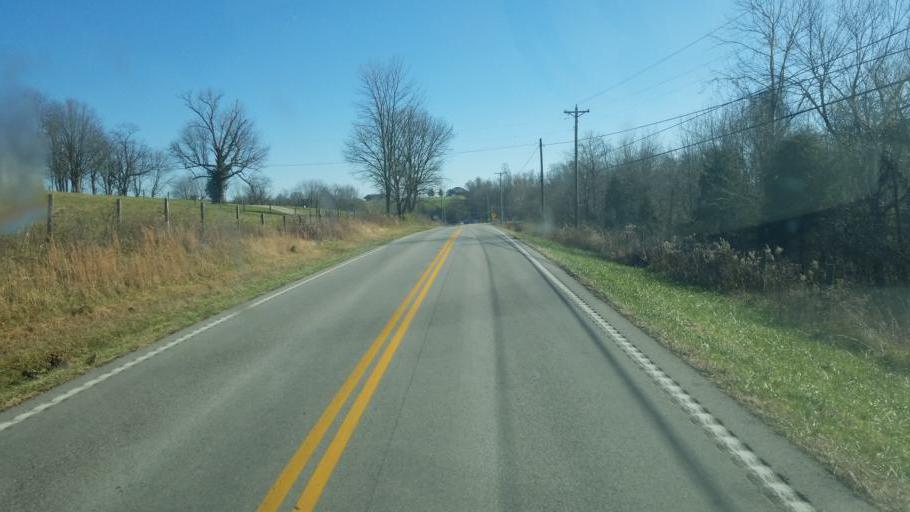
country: US
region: Kentucky
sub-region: Fleming County
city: Flemingsburg
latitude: 38.5280
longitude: -83.6181
